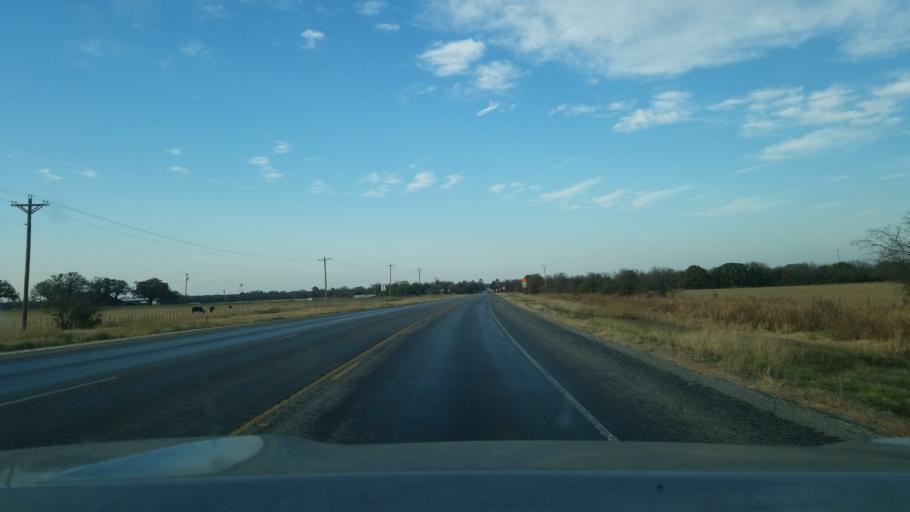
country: US
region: Texas
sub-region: Brown County
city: Lake Brownwood
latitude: 32.0792
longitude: -98.9640
